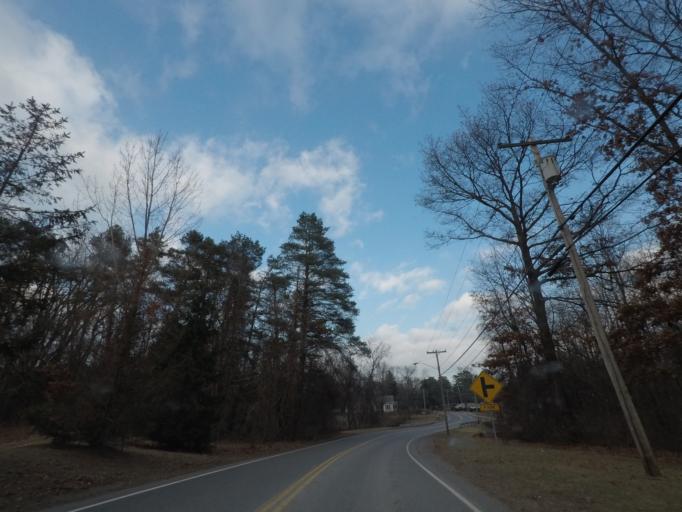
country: US
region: New York
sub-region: Albany County
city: Colonie
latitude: 42.7098
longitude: -73.8402
